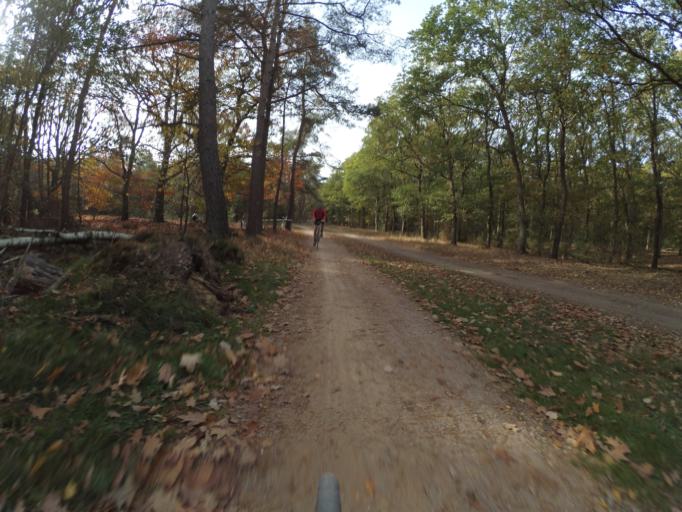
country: NL
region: Overijssel
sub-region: Gemeente Raalte
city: Raalte
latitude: 52.3584
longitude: 6.4030
